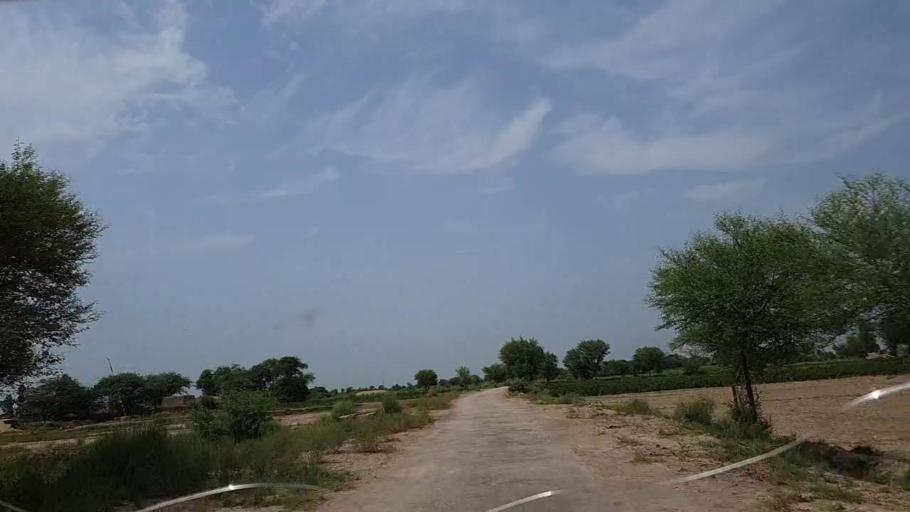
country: PK
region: Sindh
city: Tharu Shah
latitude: 26.8995
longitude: 68.0753
